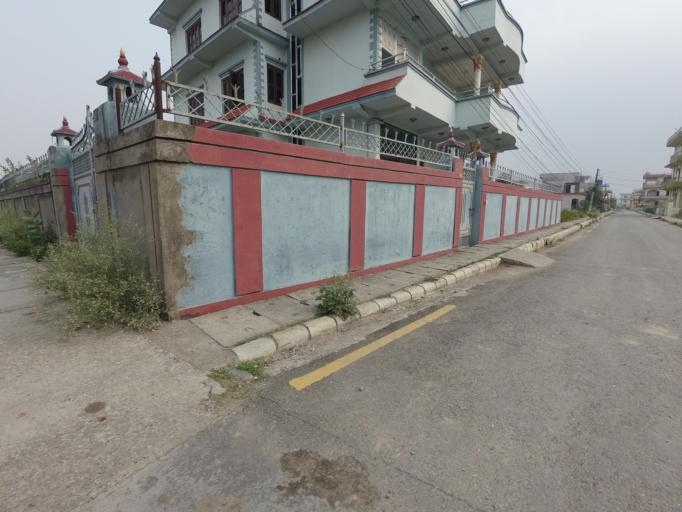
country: NP
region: Western Region
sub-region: Lumbini Zone
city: Bhairahawa
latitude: 27.5210
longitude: 83.4487
